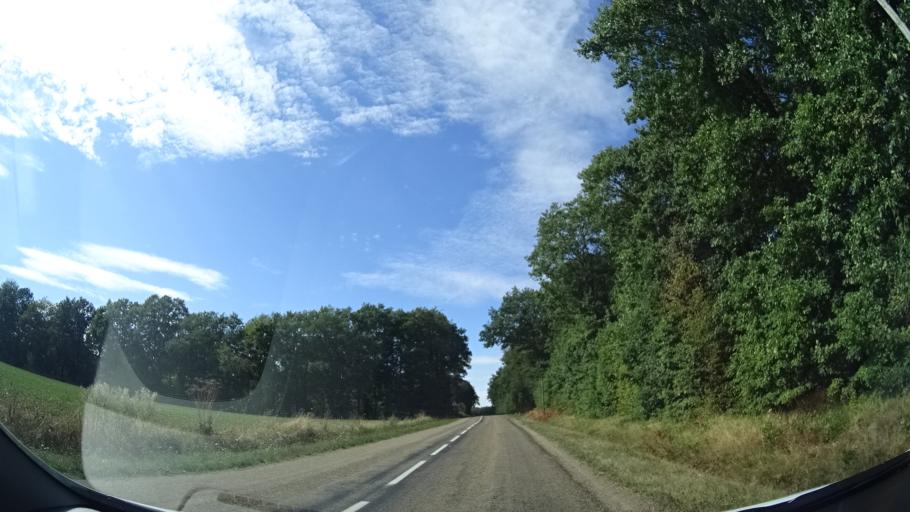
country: FR
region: Bourgogne
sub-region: Departement de l'Yonne
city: Aillant-sur-Tholon
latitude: 47.9191
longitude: 3.3079
